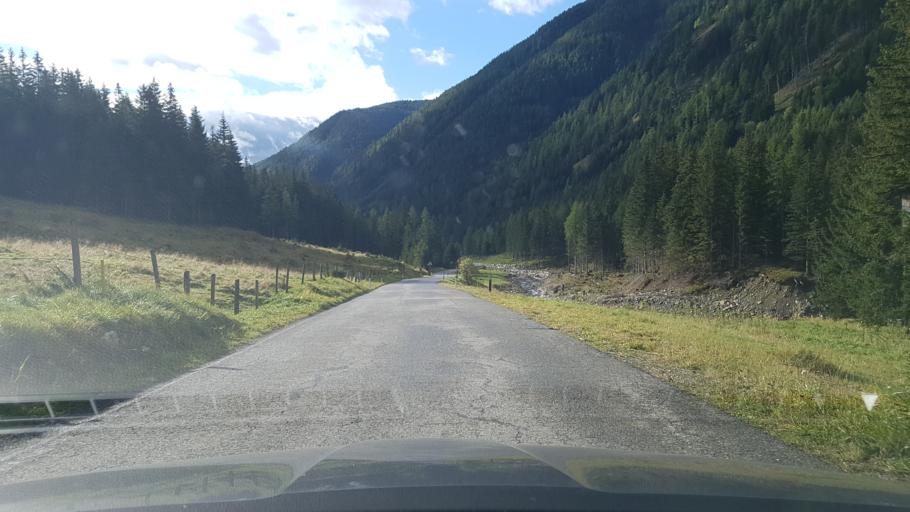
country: AT
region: Styria
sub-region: Politischer Bezirk Murau
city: Schoder
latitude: 47.2468
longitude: 14.0825
